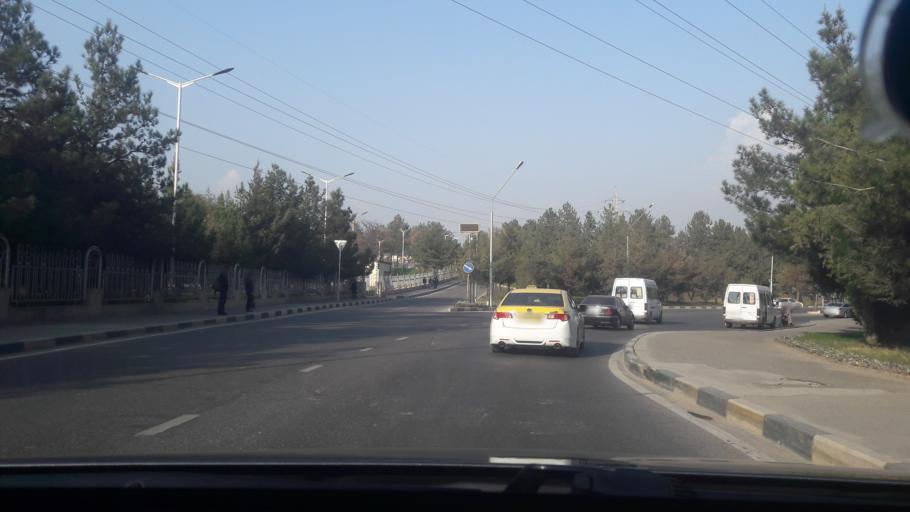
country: TJ
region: Dushanbe
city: Dushanbe
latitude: 38.5811
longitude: 68.7734
